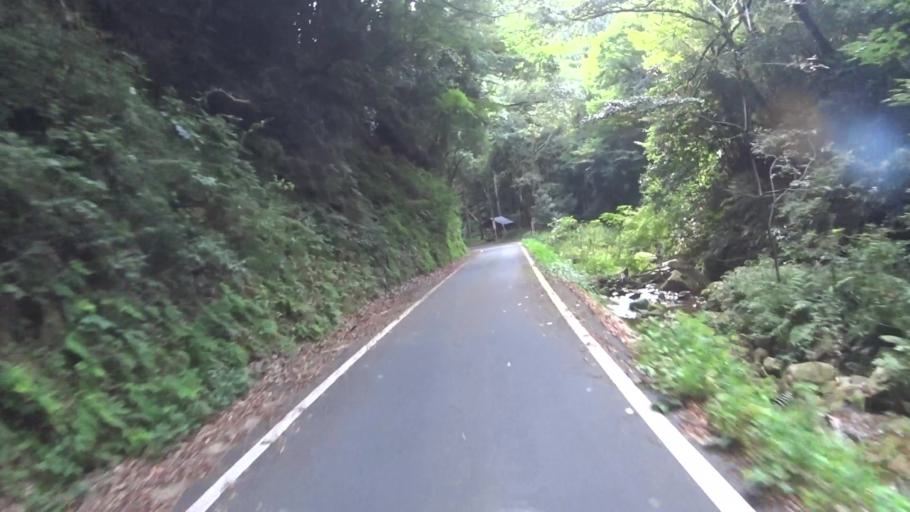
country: JP
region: Kyoto
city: Miyazu
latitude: 35.6109
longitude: 135.2058
